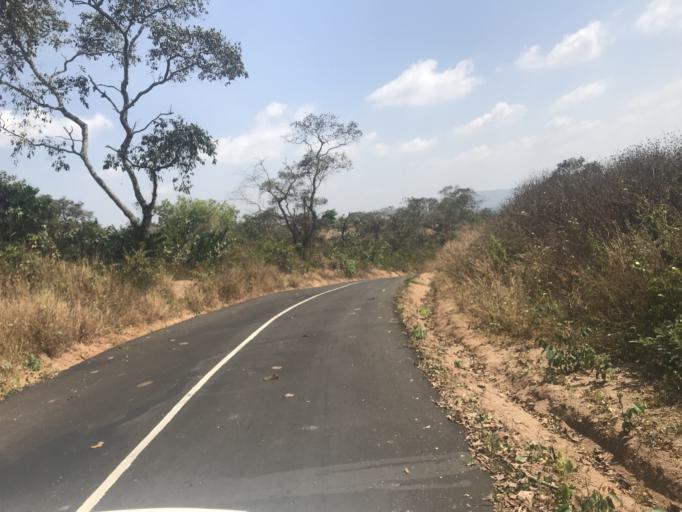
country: NG
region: Osun
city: Otan Ayegbaju
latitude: 7.8965
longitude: 4.8398
